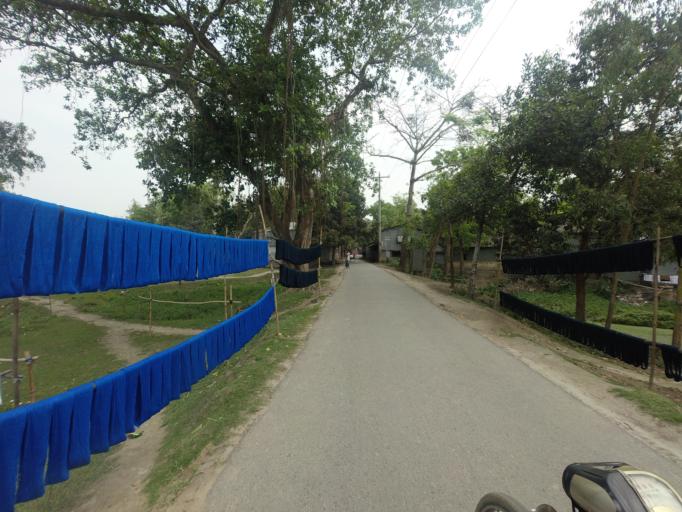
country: BD
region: Rajshahi
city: Sirajganj
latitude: 24.3316
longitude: 89.6814
